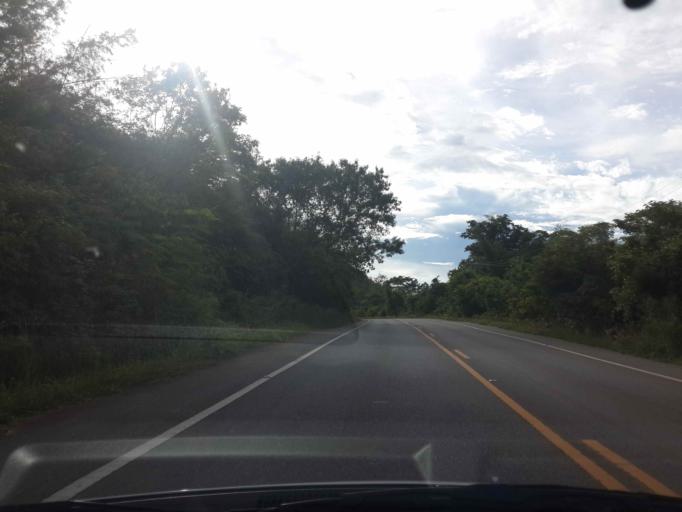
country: TH
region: Kanchanaburi
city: Sai Yok
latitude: 13.9279
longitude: 99.1205
